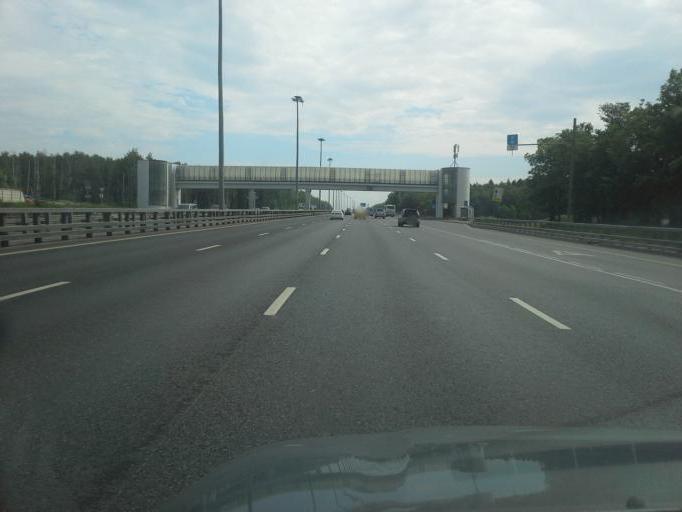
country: RU
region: Moskovskaya
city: Annino
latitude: 55.5850
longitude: 37.2620
